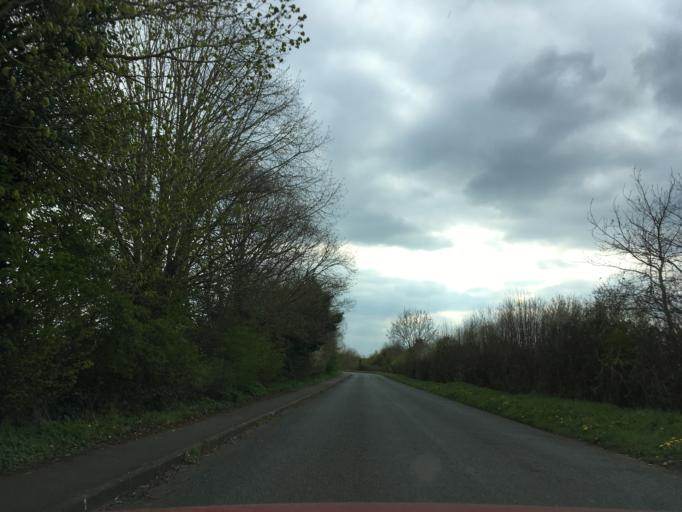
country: GB
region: England
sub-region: Oxfordshire
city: Bicester
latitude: 51.9181
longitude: -1.1521
